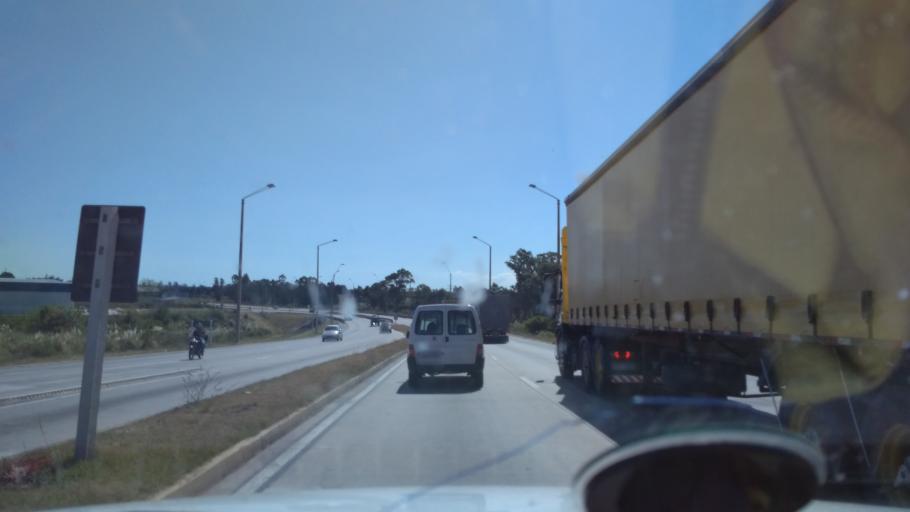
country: UY
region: Canelones
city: Toledo
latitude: -34.7905
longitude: -56.1066
